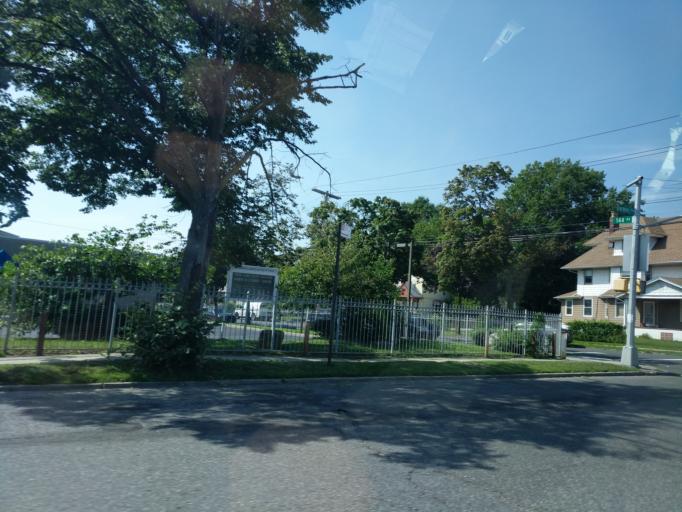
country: US
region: New York
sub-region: Queens County
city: Jamaica
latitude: 40.6683
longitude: -73.7663
